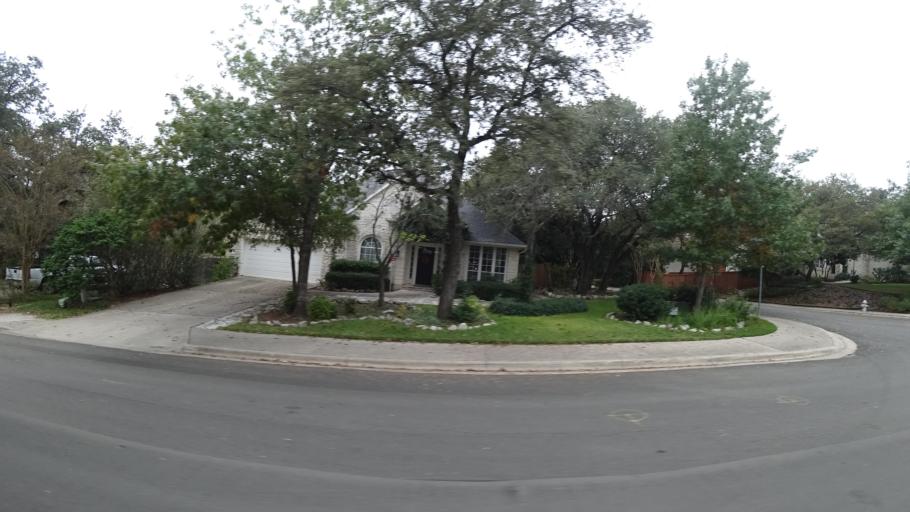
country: US
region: Texas
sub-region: Williamson County
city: Anderson Mill
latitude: 30.4359
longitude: -97.8296
